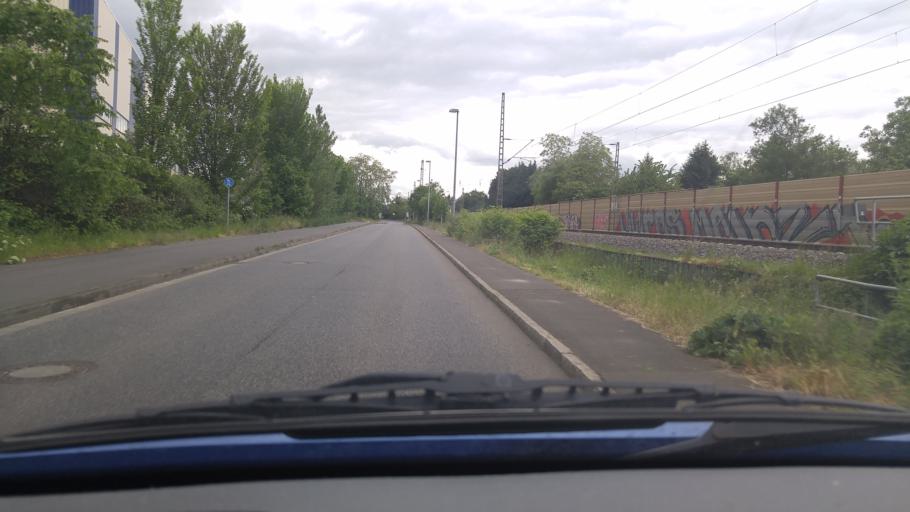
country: DE
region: Hesse
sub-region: Regierungsbezirk Darmstadt
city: Hochheim am Main
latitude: 50.0057
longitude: 8.3130
